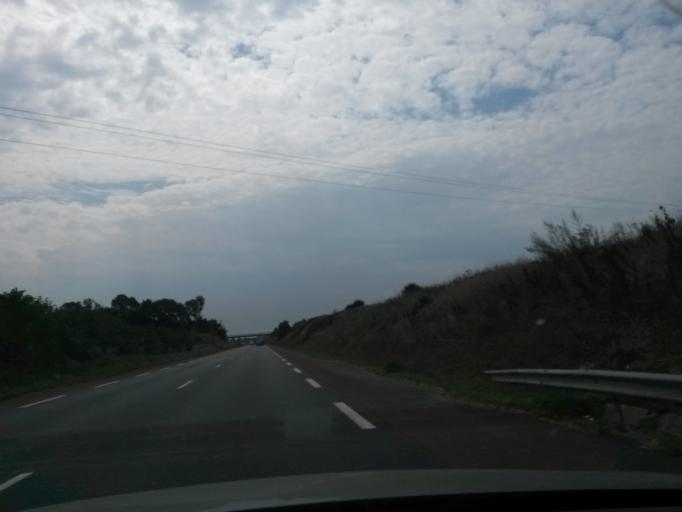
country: FR
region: Poitou-Charentes
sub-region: Departement de la Charente-Maritime
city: Saint-Xandre
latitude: 46.1884
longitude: -1.0939
